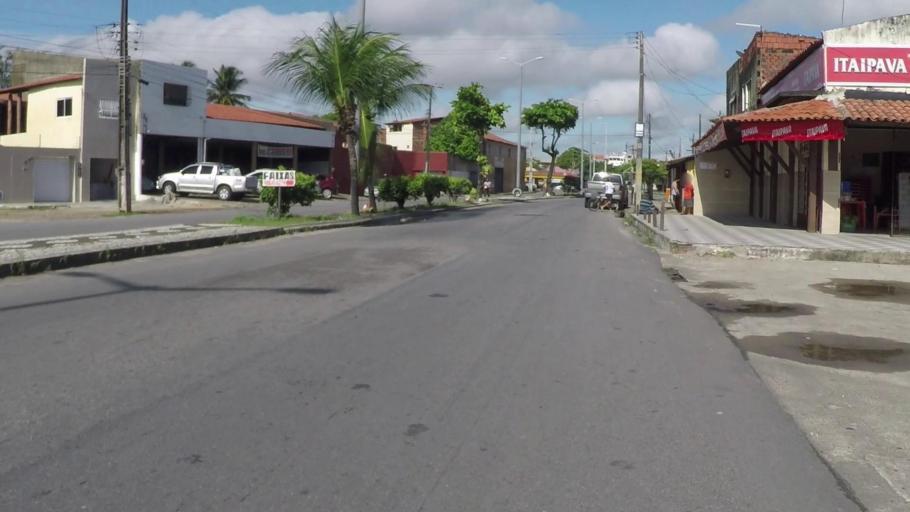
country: BR
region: Ceara
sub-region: Fortaleza
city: Fortaleza
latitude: -3.7023
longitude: -38.5907
